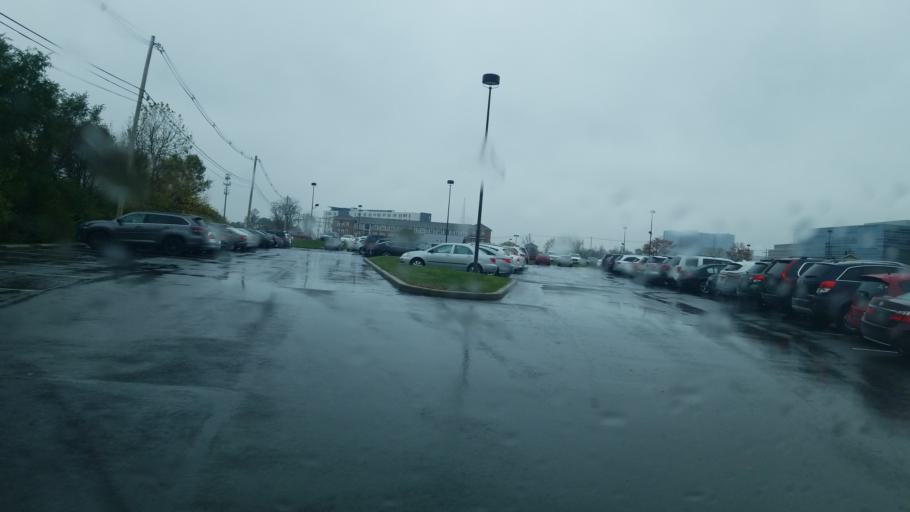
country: US
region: Ohio
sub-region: Franklin County
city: Grandview Heights
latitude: 39.9818
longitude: -83.0248
